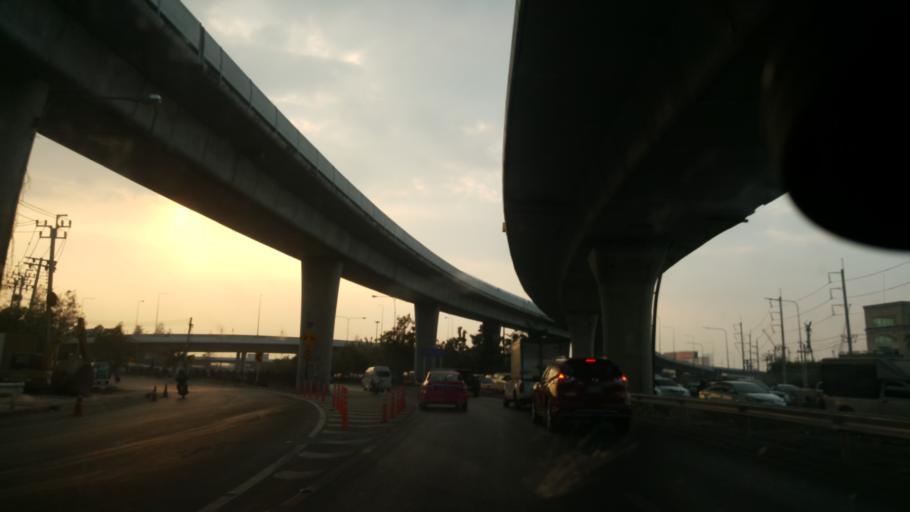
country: TH
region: Bangkok
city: Bangkok Yai
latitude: 13.7144
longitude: 100.4639
